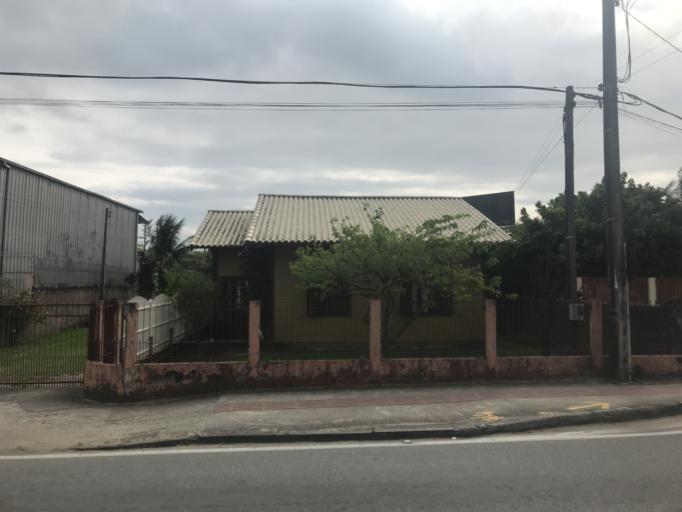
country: BR
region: Santa Catarina
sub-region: Florianopolis
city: Costeira do Pirajubae
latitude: -27.6474
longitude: -48.5216
